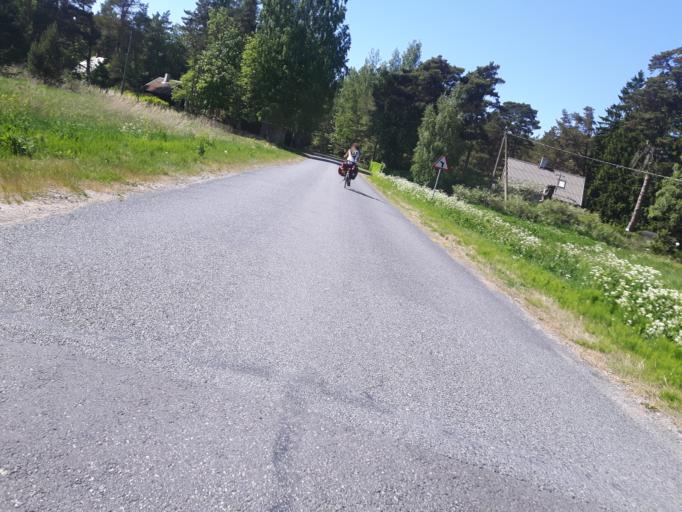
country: EE
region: Laeaene-Virumaa
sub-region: Haljala vald
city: Haljala
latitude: 59.5766
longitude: 26.2730
